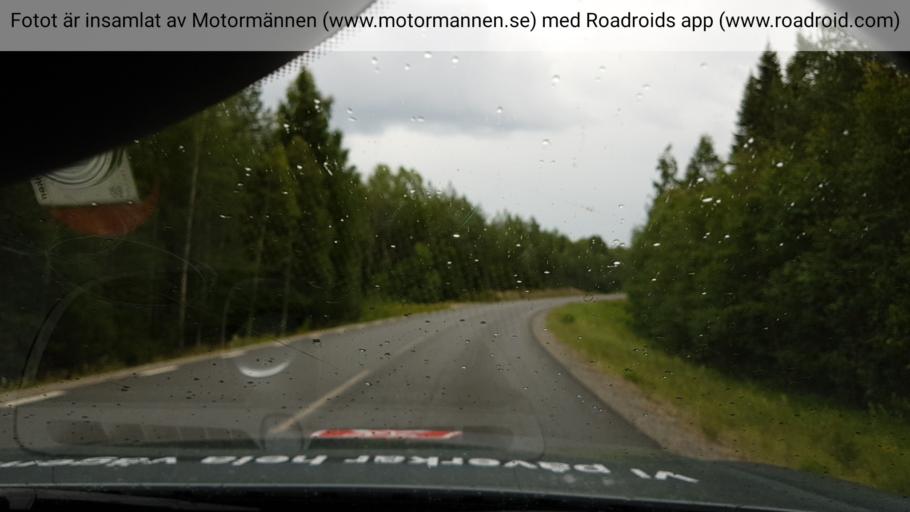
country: SE
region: Jaemtland
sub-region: Braecke Kommun
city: Braecke
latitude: 62.4171
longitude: 15.0121
